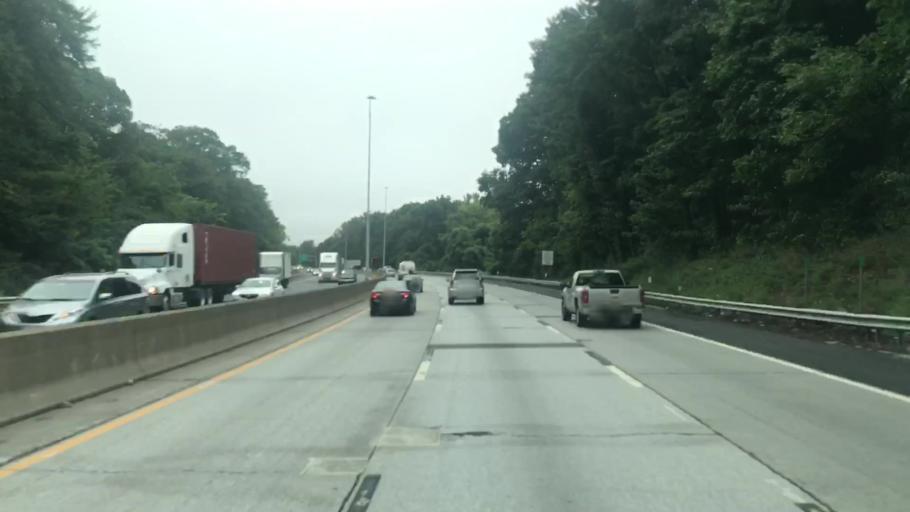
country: US
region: New York
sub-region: Westchester County
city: Harrison
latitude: 40.9662
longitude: -73.7274
